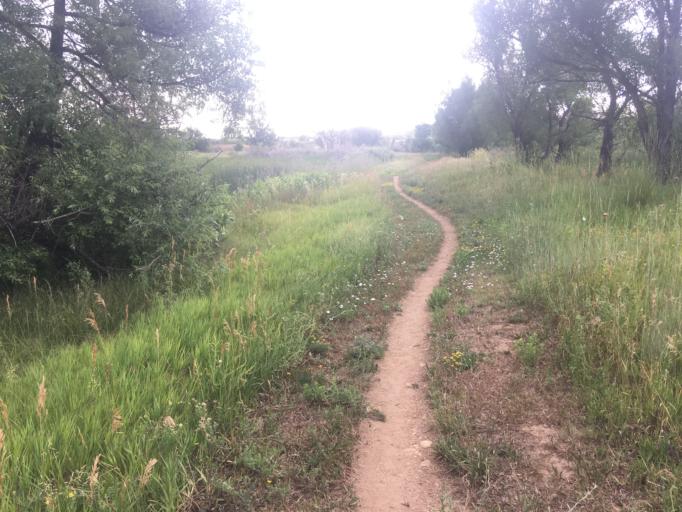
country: US
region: Colorado
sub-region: Boulder County
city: Boulder
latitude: 39.9685
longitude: -105.2301
